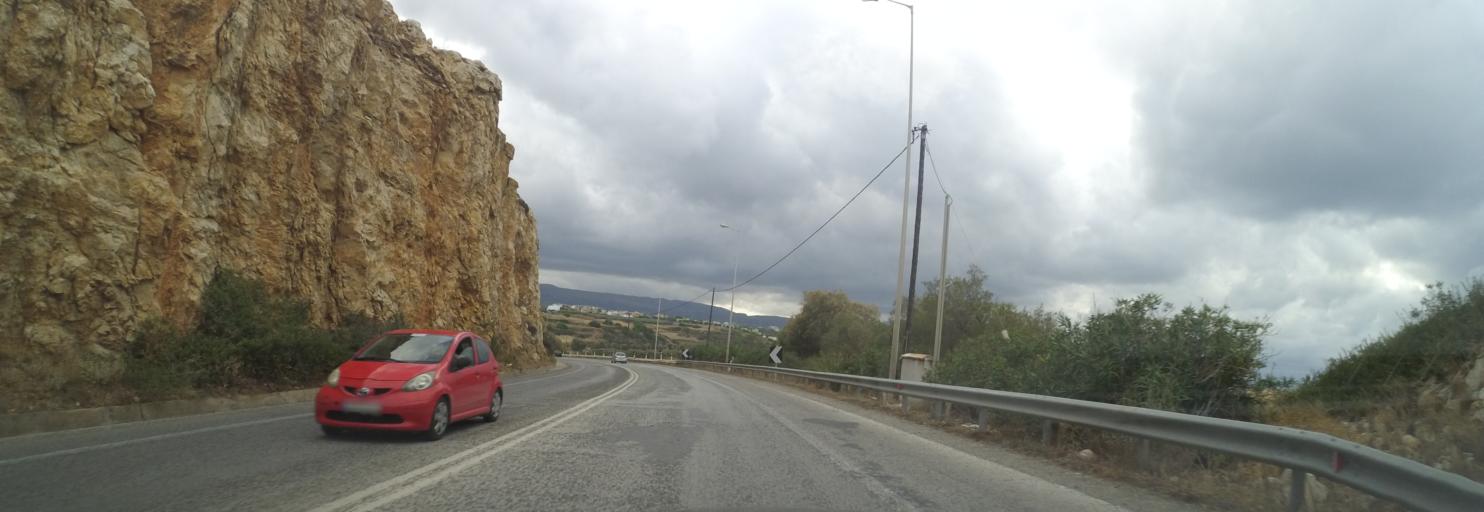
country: GR
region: Crete
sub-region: Nomos Rethymnis
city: Panormos
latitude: 35.3978
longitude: 24.6181
